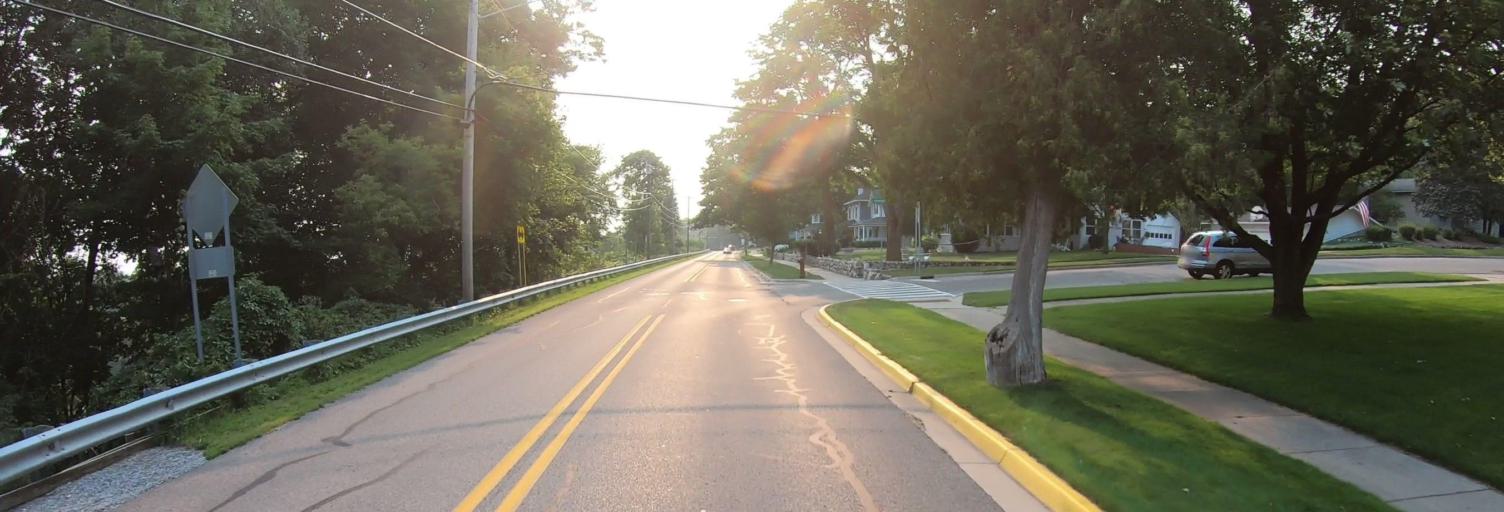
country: US
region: Michigan
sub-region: Emmet County
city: Harbor Springs
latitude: 45.4316
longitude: -84.9929
